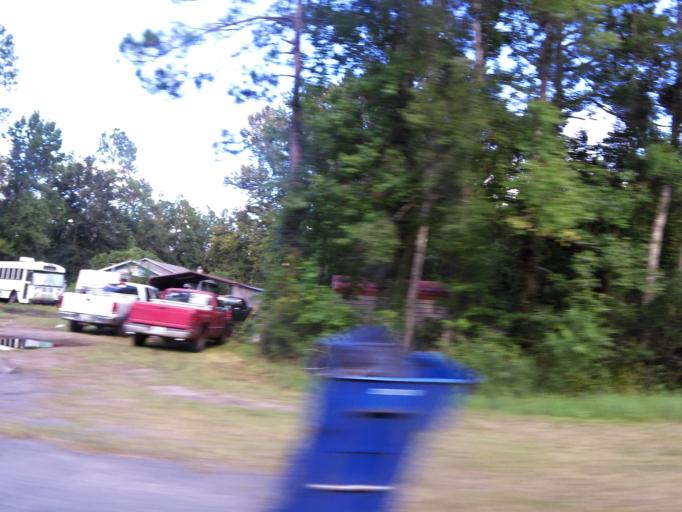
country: US
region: Georgia
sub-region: Camden County
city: Woodbine
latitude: 30.9413
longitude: -81.7182
